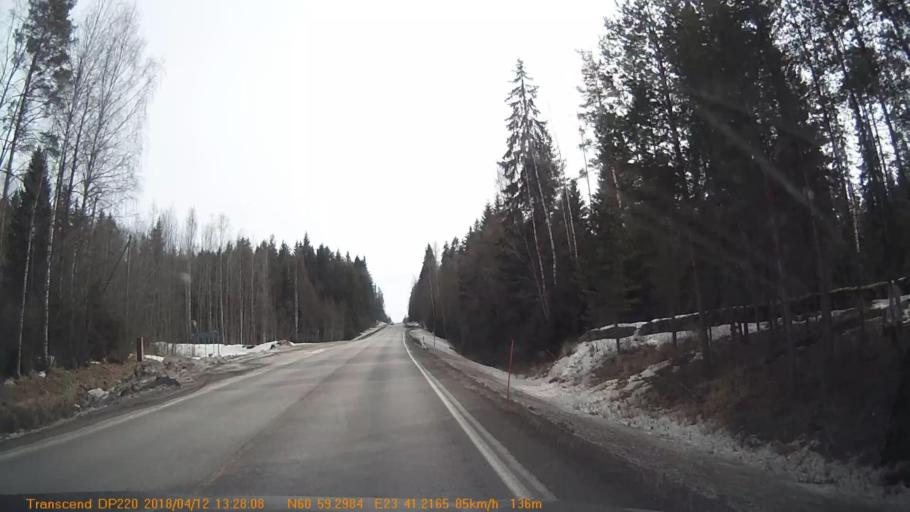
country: FI
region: Pirkanmaa
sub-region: Etelae-Pirkanmaa
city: Kylmaekoski
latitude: 60.9880
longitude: 23.6872
